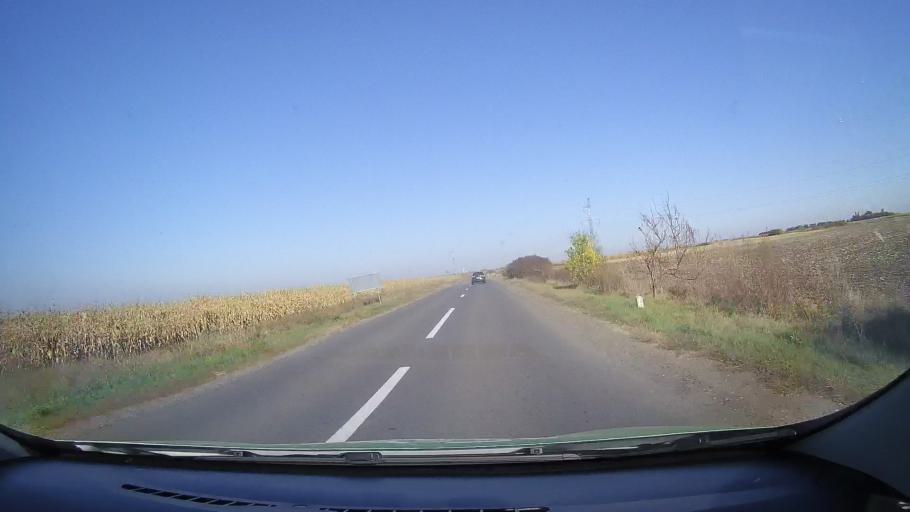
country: RO
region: Satu Mare
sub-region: Comuna Cauas
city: Cauas
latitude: 47.6048
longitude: 22.5427
